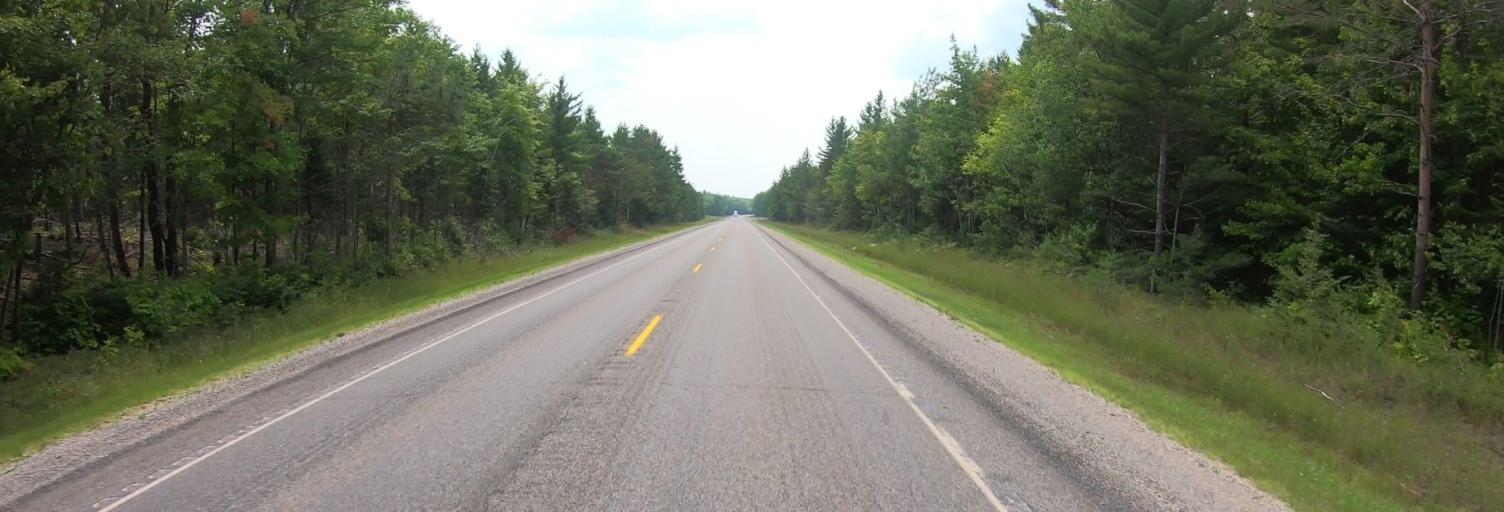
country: US
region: Michigan
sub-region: Alger County
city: Munising
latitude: 46.3437
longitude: -86.7301
